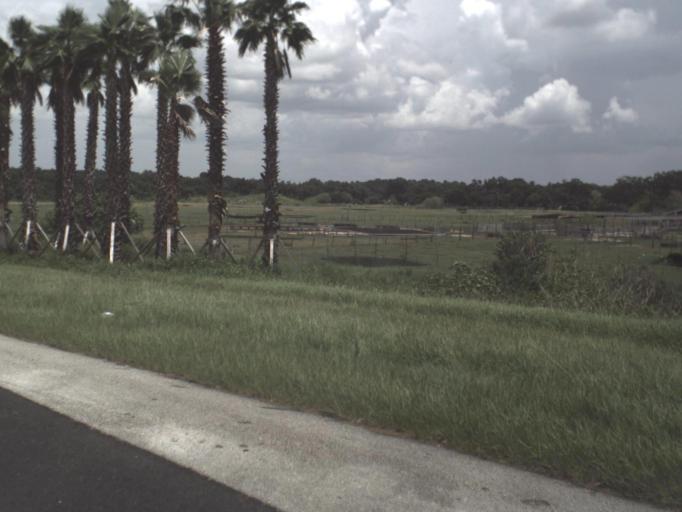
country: US
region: Florida
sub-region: Hillsborough County
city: East Lake-Orient Park
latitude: 27.9980
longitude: -82.3572
